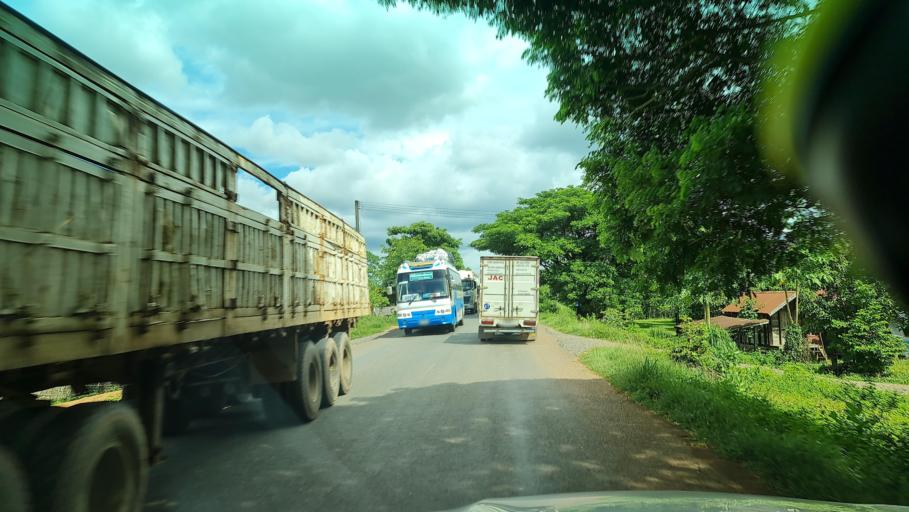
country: LA
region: Bolikhamxai
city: Ban Nahin
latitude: 18.1911
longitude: 104.2221
